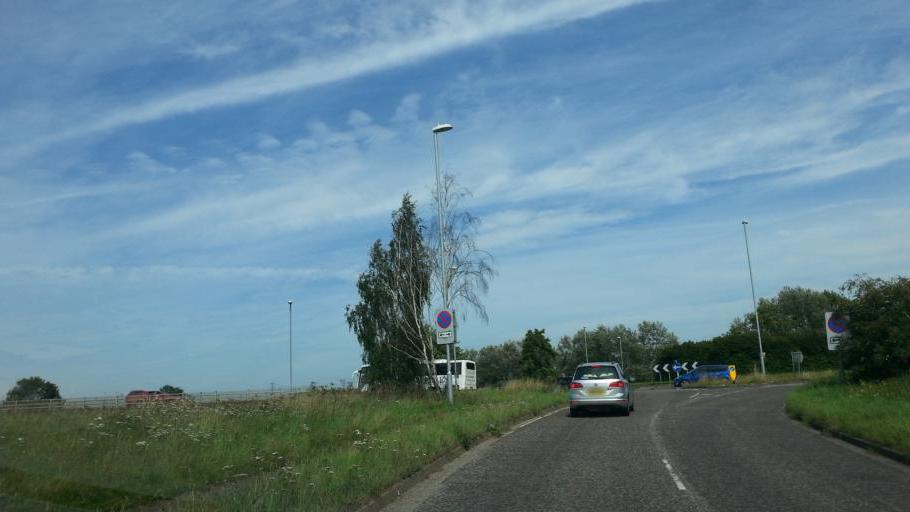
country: GB
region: England
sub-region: Cambridgeshire
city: Littleport
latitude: 52.4642
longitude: 0.3215
